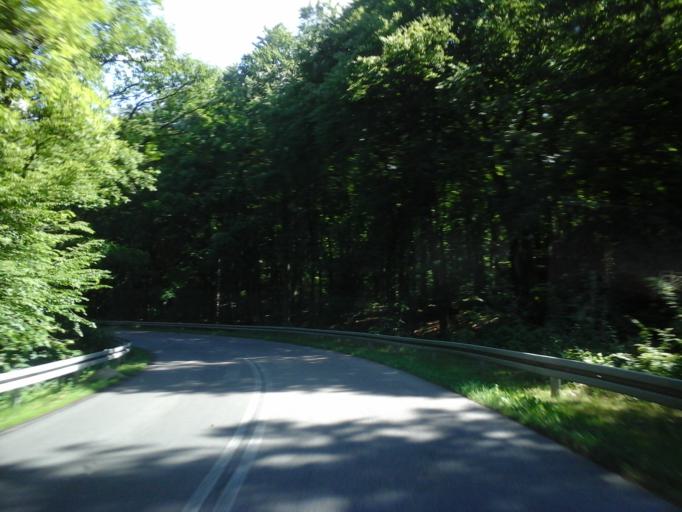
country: PL
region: West Pomeranian Voivodeship
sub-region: Powiat lobeski
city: Lobez
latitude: 53.5976
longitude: 15.6166
